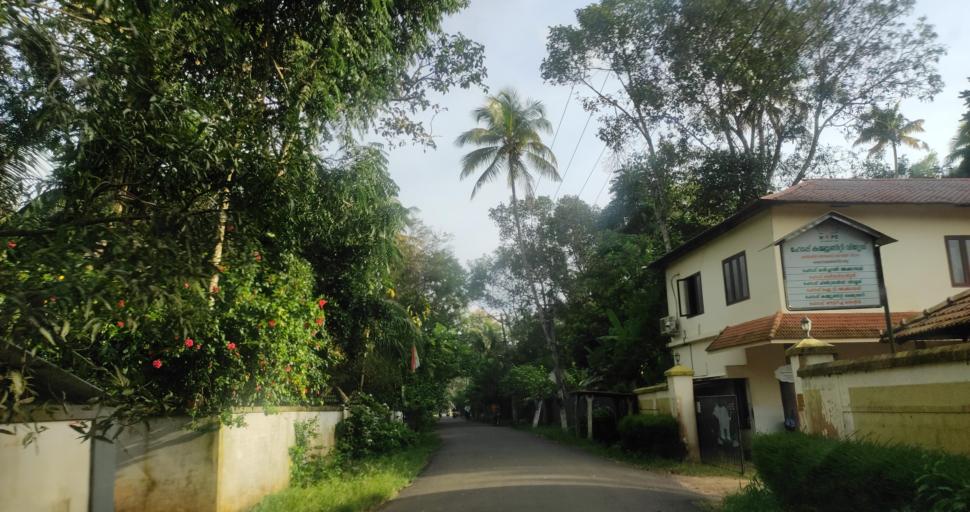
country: IN
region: Kerala
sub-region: Alappuzha
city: Shertallai
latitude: 9.6138
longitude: 76.3405
